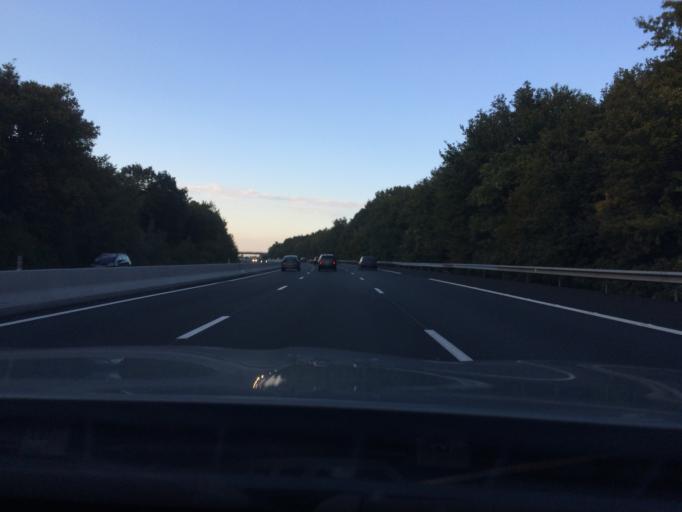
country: FR
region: Ile-de-France
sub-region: Departement de l'Essonne
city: Soisy-sur-Ecole
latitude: 48.5027
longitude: 2.5129
